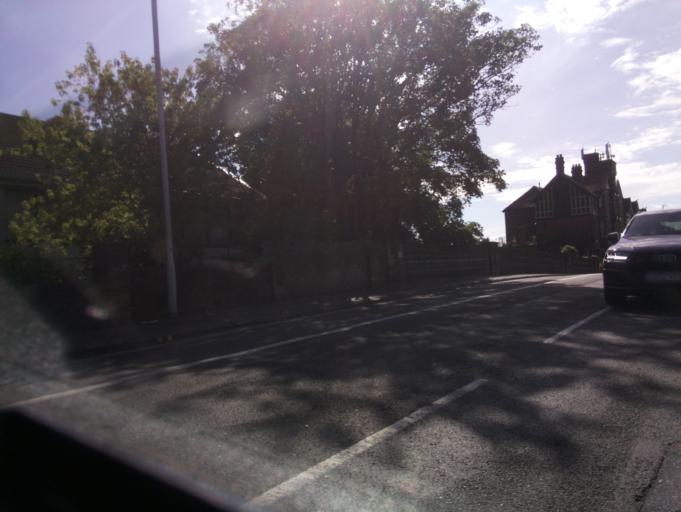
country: GB
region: England
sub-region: Dorset
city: Parkstone
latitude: 50.7268
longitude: -1.9199
